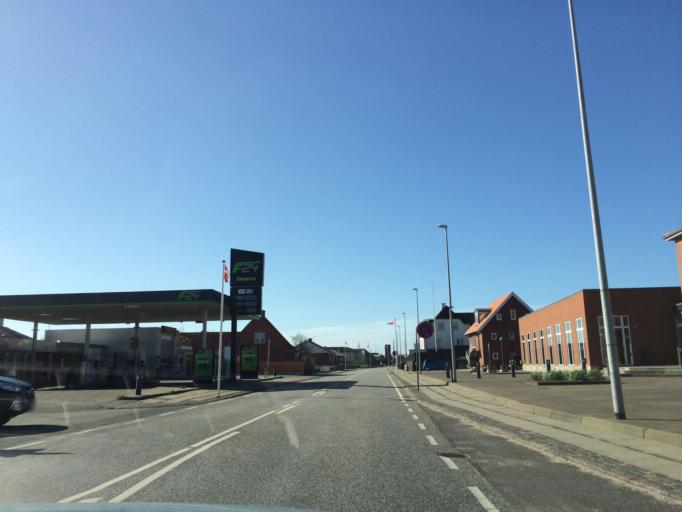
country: DK
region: Central Jutland
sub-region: Ringkobing-Skjern Kommune
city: Hvide Sande
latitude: 56.0079
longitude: 8.1297
